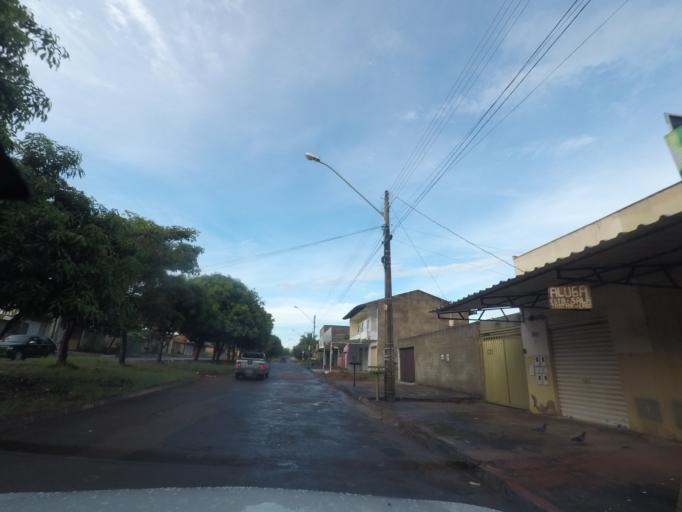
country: BR
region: Goias
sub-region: Goiania
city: Goiania
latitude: -16.7436
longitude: -49.3722
